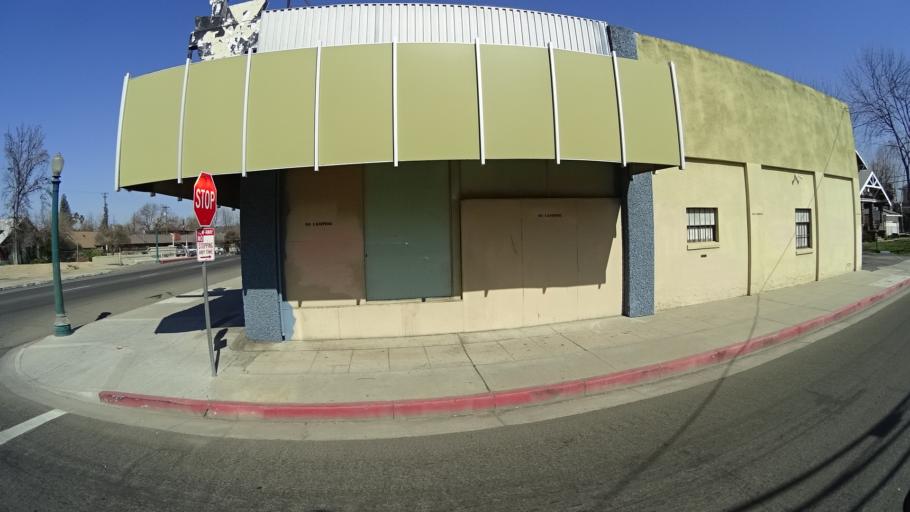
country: US
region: California
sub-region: Fresno County
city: Fresno
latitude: 36.7530
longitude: -119.8002
